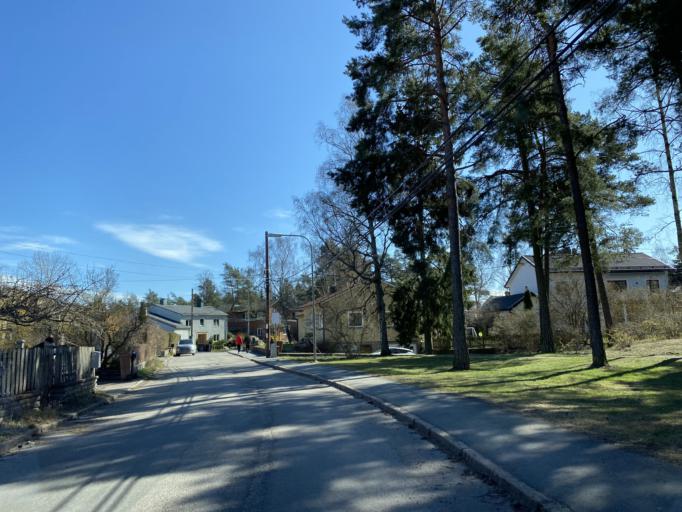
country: SE
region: Stockholm
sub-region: Stockholms Kommun
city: Arsta
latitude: 59.2823
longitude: 18.0538
